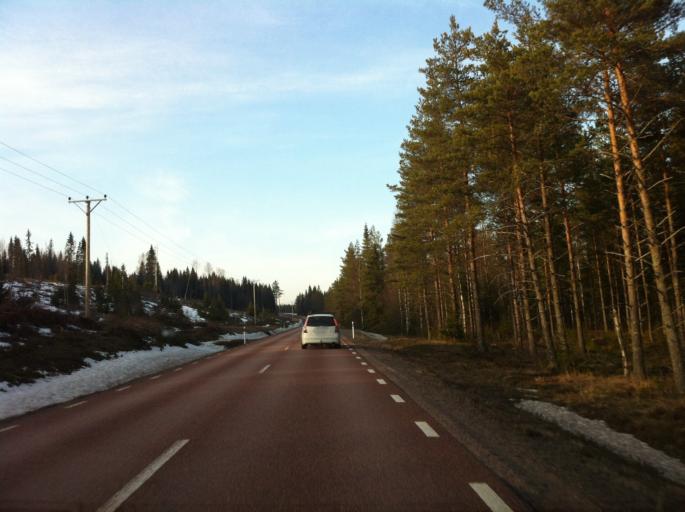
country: SE
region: Vaermland
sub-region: Filipstads Kommun
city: Lesjofors
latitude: 60.1878
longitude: 14.1968
